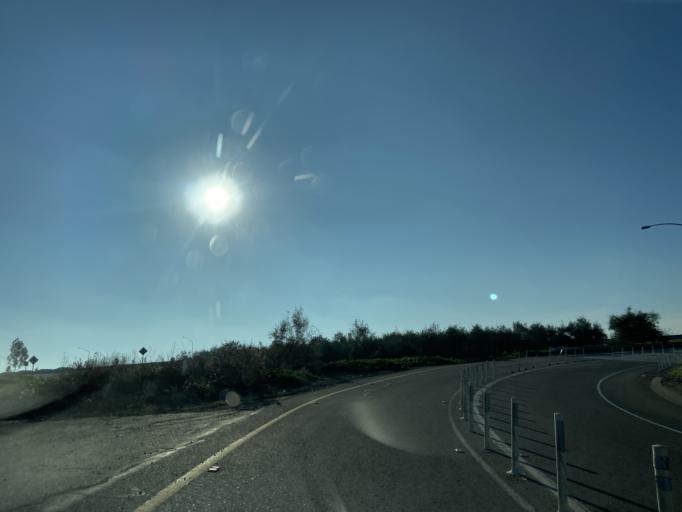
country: US
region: California
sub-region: San Diego County
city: Bonita
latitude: 32.6302
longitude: -116.9700
